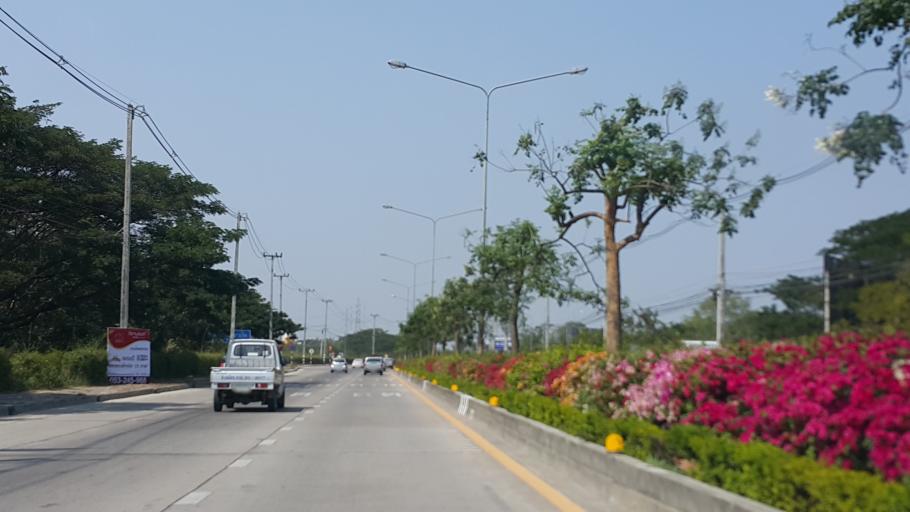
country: TH
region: Chiang Mai
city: Chiang Mai
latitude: 18.7941
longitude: 99.0371
